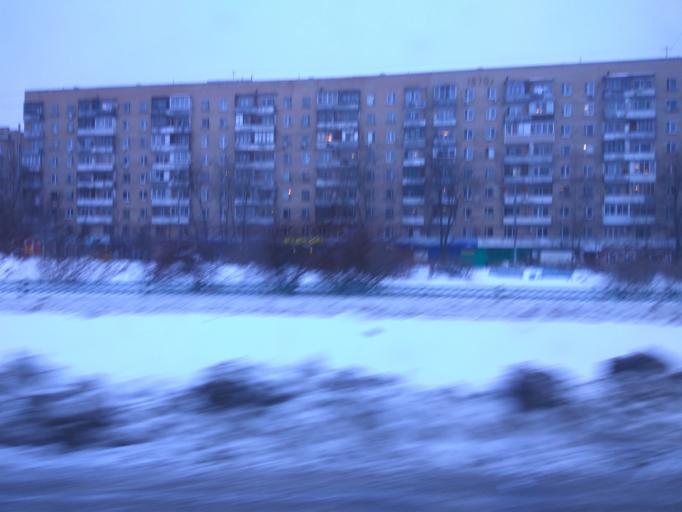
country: RU
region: Moscow
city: Gol'yanovo
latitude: 55.8190
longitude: 37.8264
